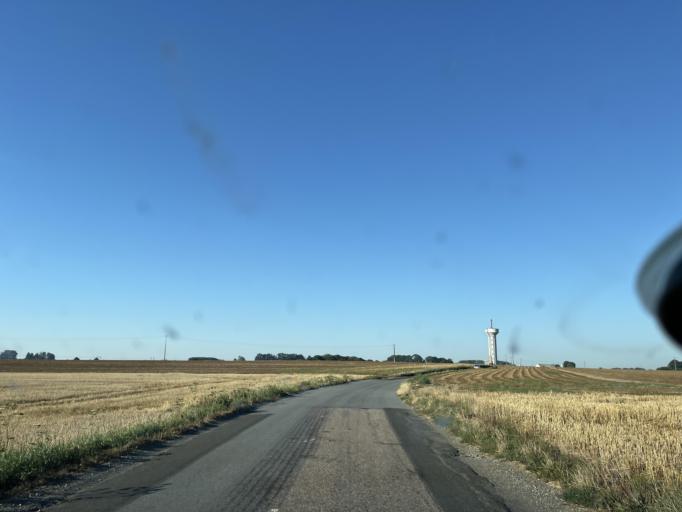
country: FR
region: Haute-Normandie
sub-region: Departement de la Seine-Maritime
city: Fauville-en-Caux
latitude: 49.6156
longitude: 0.6099
